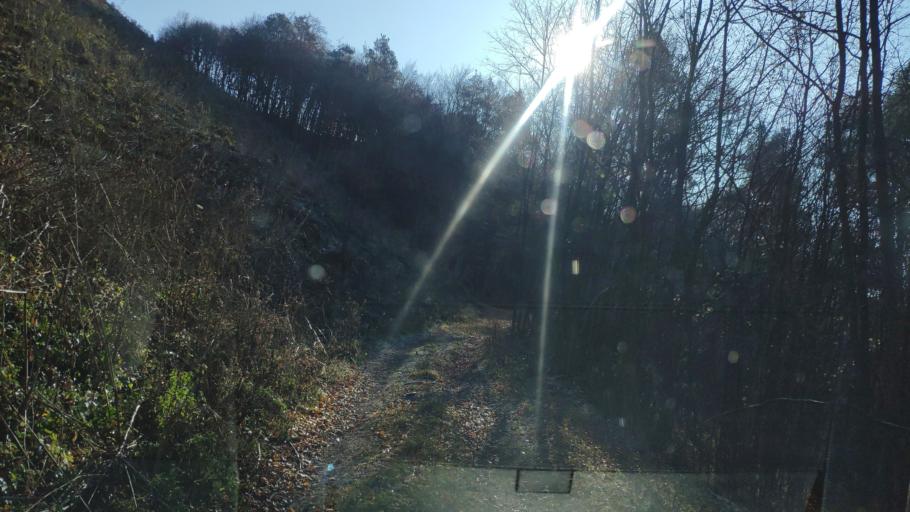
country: SK
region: Presovsky
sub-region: Okres Presov
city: Presov
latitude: 48.8999
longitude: 21.2067
